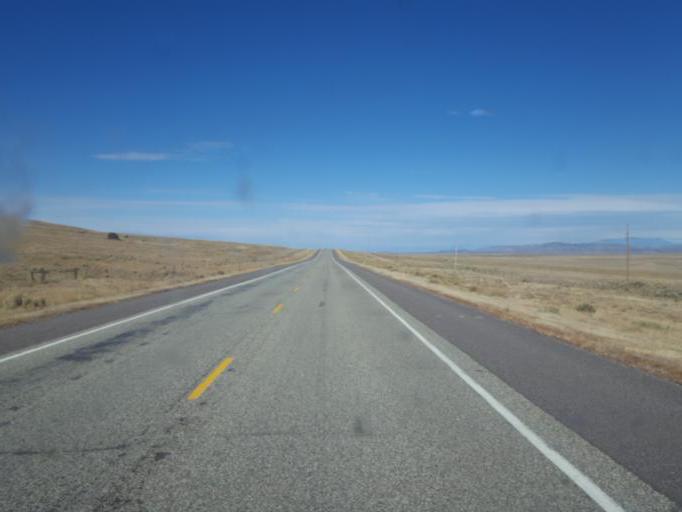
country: US
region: Colorado
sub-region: Conejos County
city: Conejos
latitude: 36.8500
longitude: -105.9722
